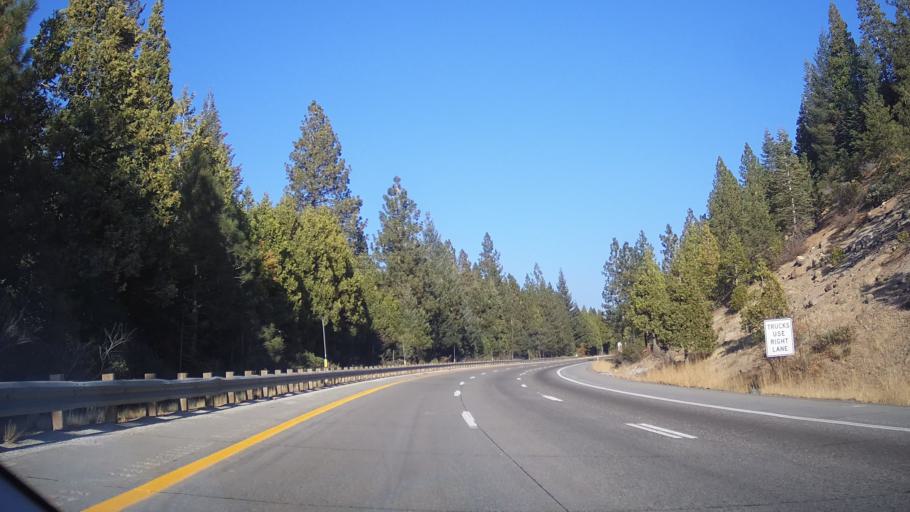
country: US
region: California
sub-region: Placer County
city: Foresthill
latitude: 39.2419
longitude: -120.7516
